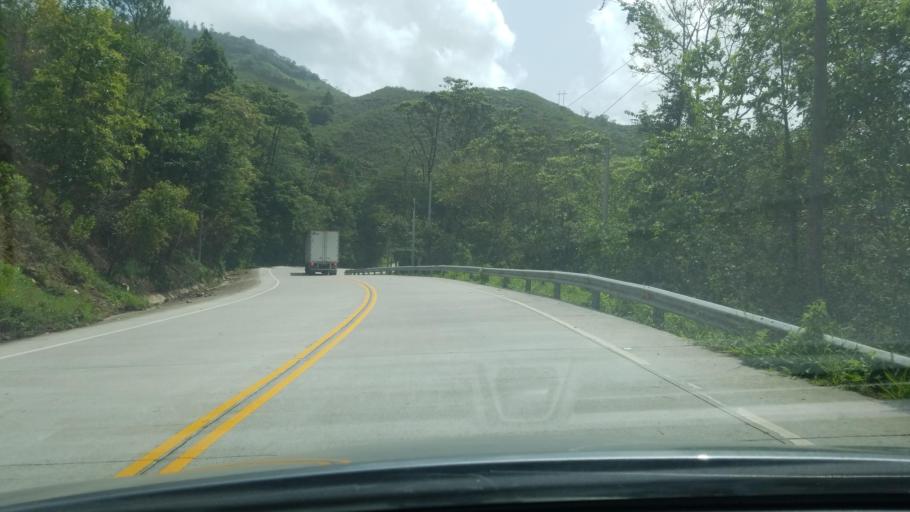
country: HN
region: Copan
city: San Jeronimo
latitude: 14.9304
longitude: -88.9450
